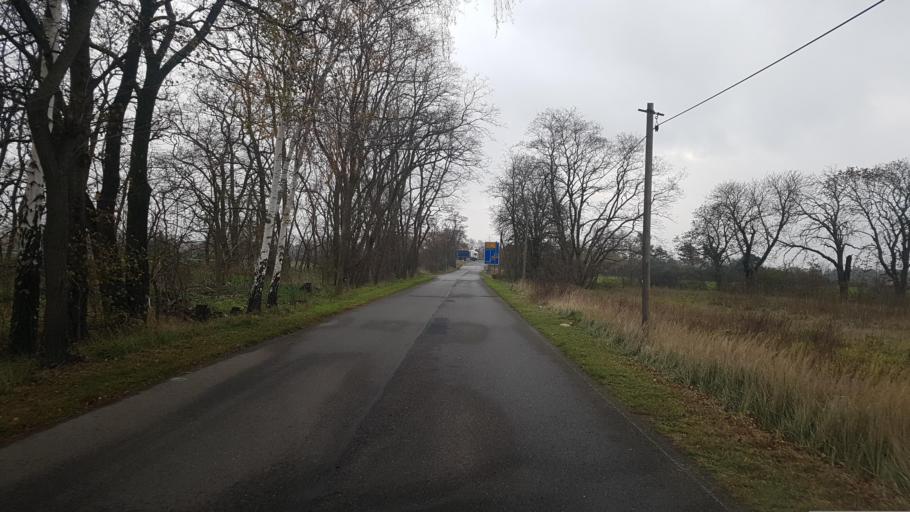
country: DE
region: Brandenburg
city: Lubbenau
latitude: 51.8339
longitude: 13.9084
